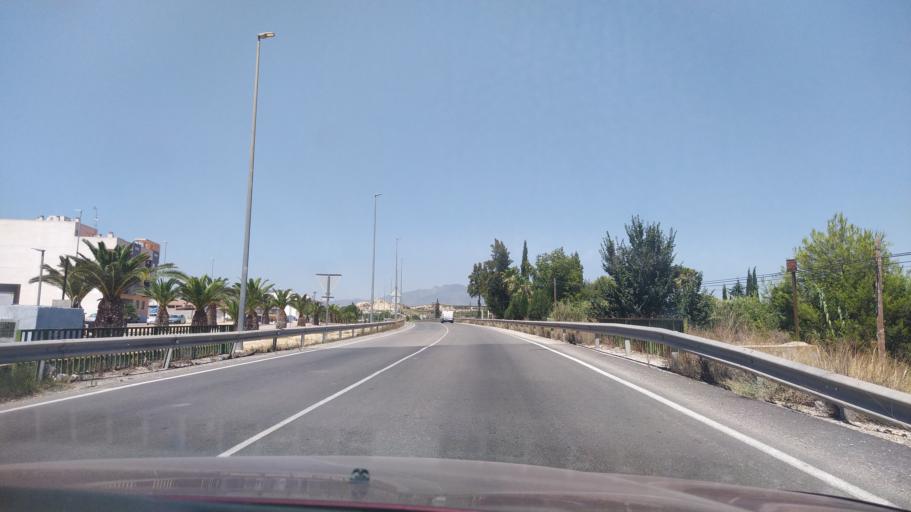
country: ES
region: Murcia
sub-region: Murcia
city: Ceuti
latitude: 38.0871
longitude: -1.2704
